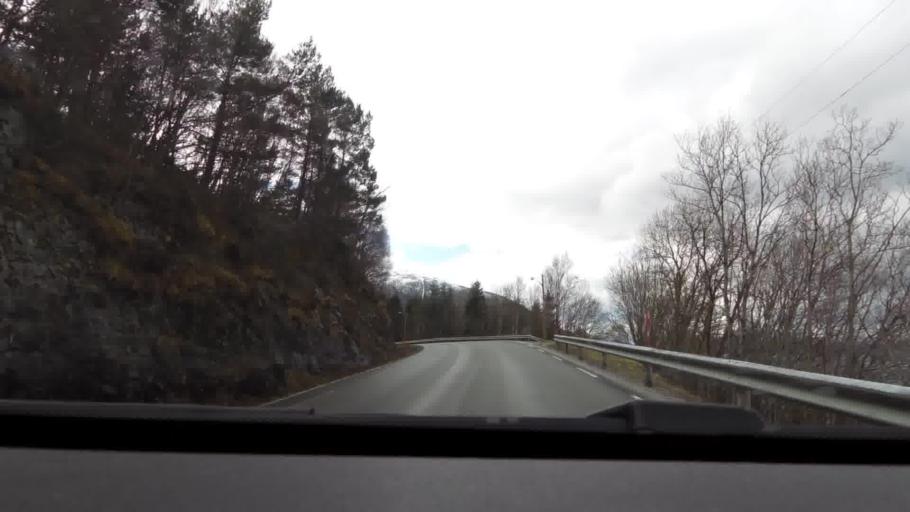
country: NO
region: More og Romsdal
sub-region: Eide
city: Eide
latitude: 62.9186
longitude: 7.5513
